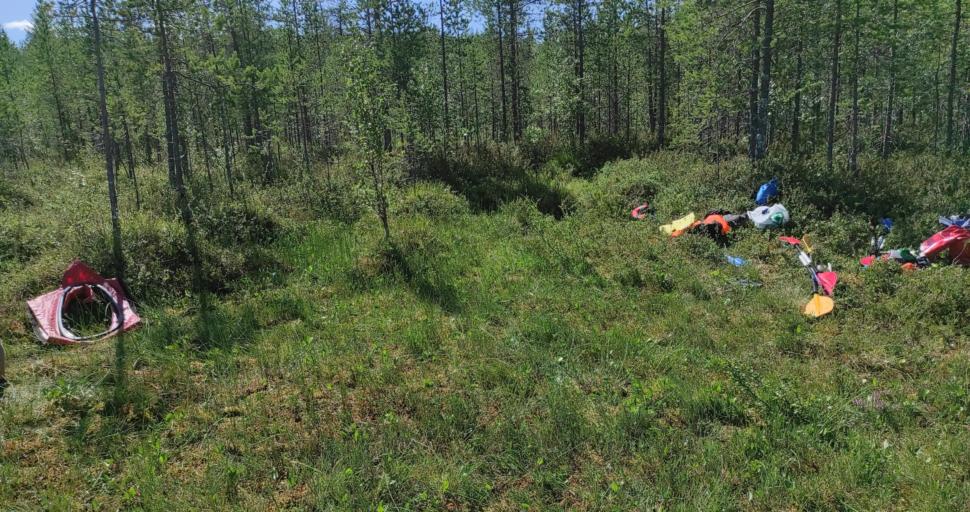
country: RU
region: Murmansk
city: Zelenoborskiy
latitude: 66.6870
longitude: 32.4584
